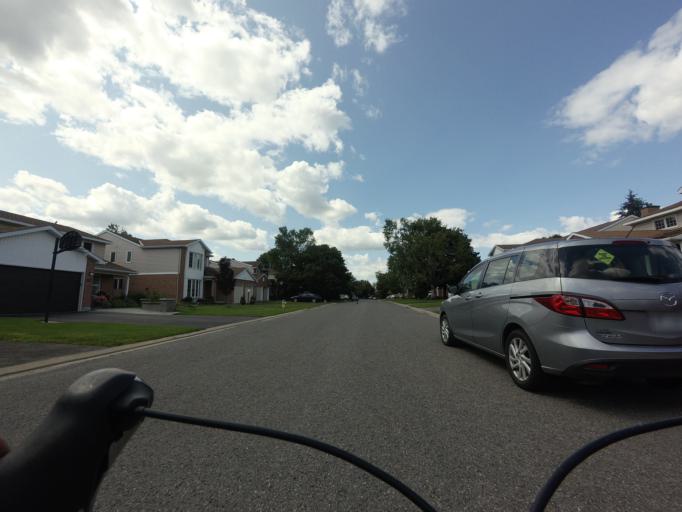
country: CA
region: Ontario
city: Bells Corners
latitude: 45.2958
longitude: -75.8627
